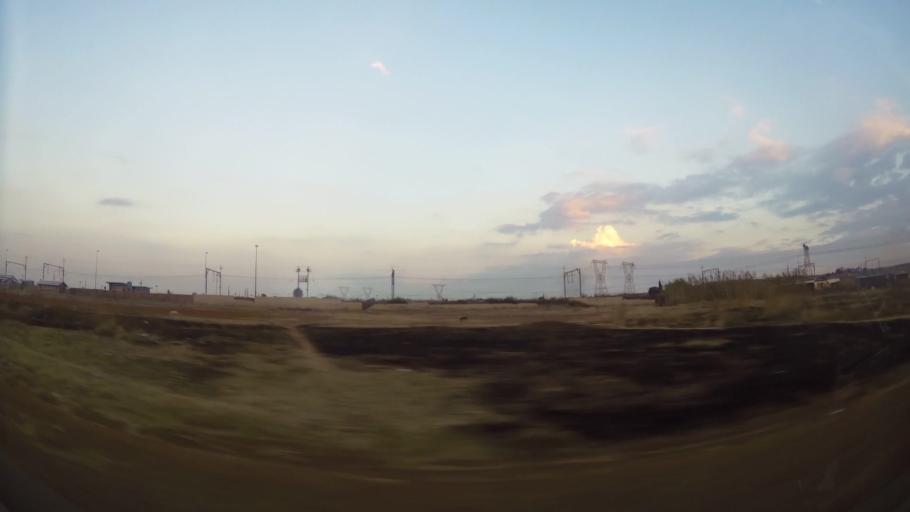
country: ZA
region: Gauteng
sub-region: City of Johannesburg Metropolitan Municipality
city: Orange Farm
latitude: -26.5584
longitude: 27.8762
